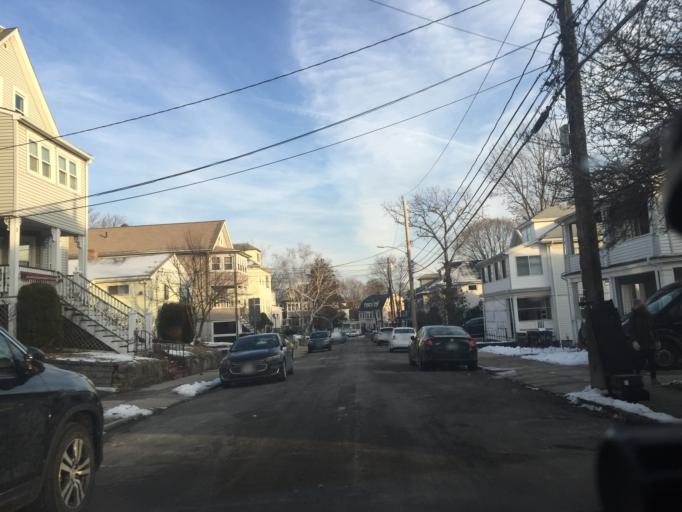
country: US
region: Massachusetts
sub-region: Middlesex County
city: Watertown
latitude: 42.3551
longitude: -71.1601
